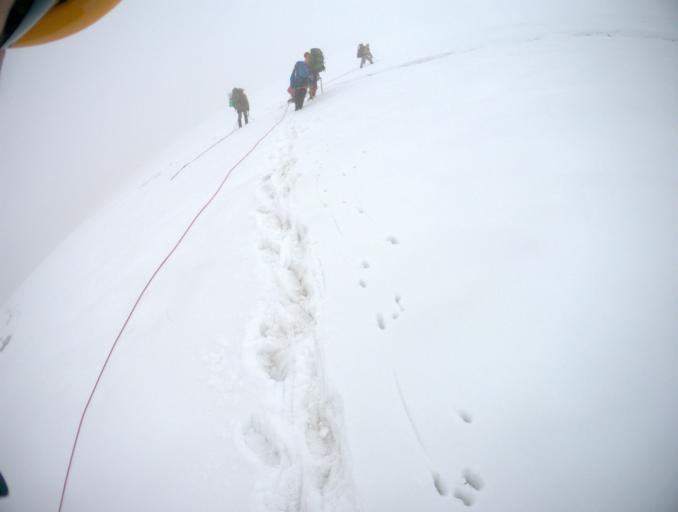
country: RU
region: Kabardino-Balkariya
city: Terskol
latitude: 43.3741
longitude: 42.4808
